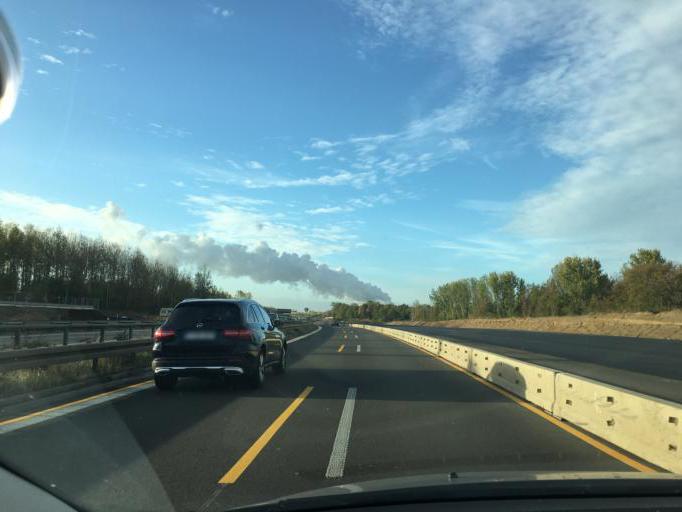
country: DE
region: Saxony
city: Bohlen
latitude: 51.2362
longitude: 12.3889
